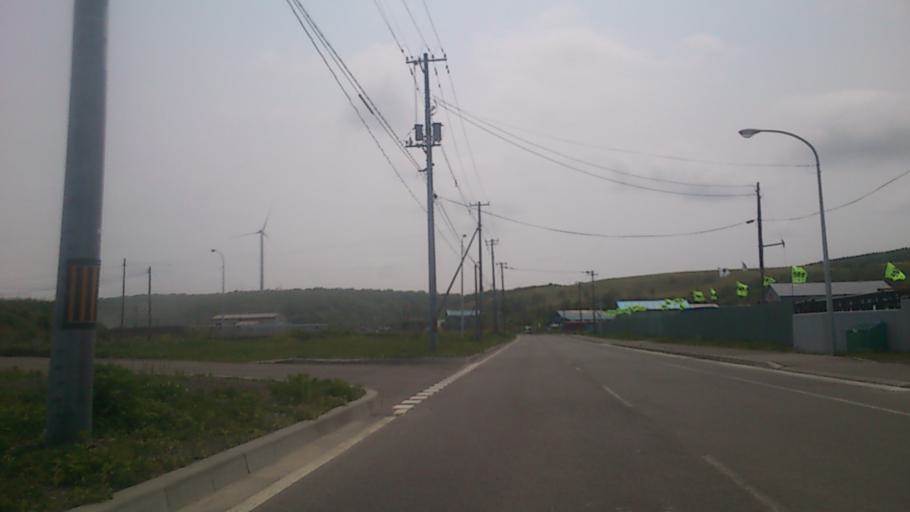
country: JP
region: Hokkaido
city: Nemuro
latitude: 43.2840
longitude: 145.5675
